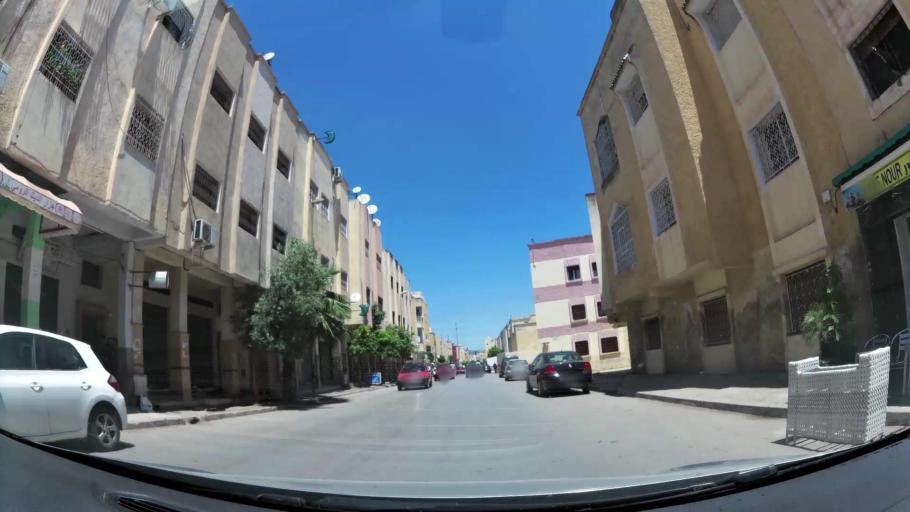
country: MA
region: Fes-Boulemane
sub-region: Fes
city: Fes
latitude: 34.0232
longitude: -5.0092
